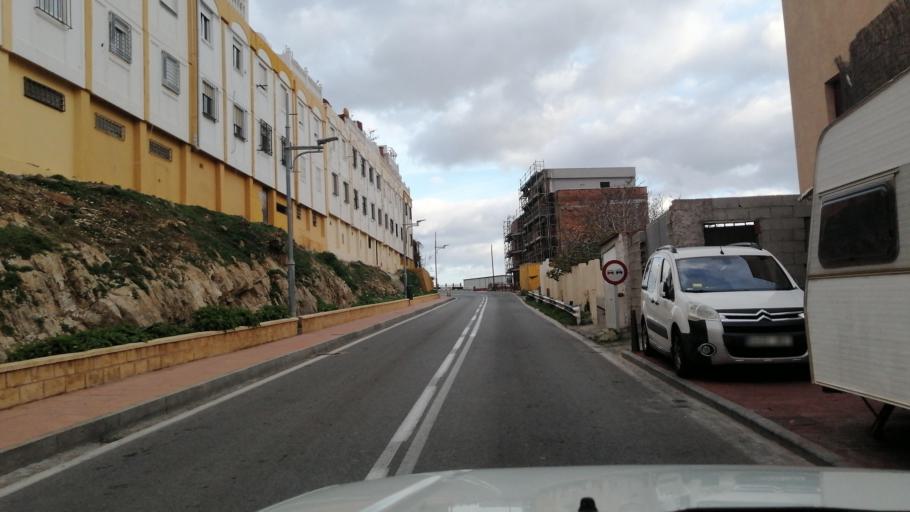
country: ES
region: Ceuta
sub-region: Ceuta
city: Ceuta
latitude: 35.8902
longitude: -5.2943
